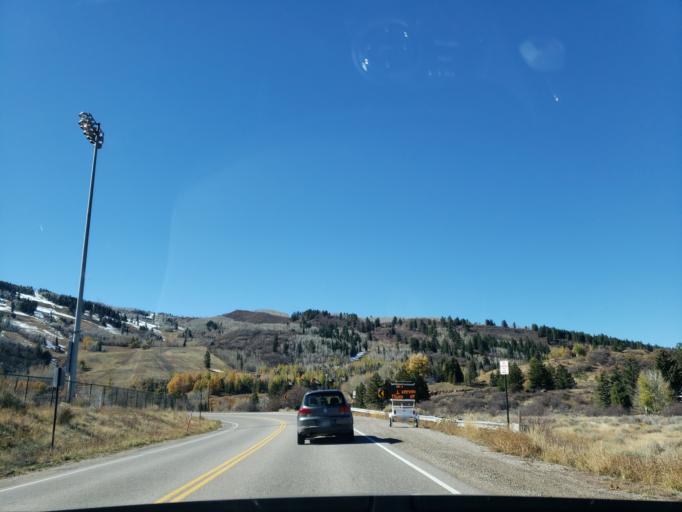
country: US
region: Colorado
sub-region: Pitkin County
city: Aspen
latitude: 39.1932
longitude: -106.8487
